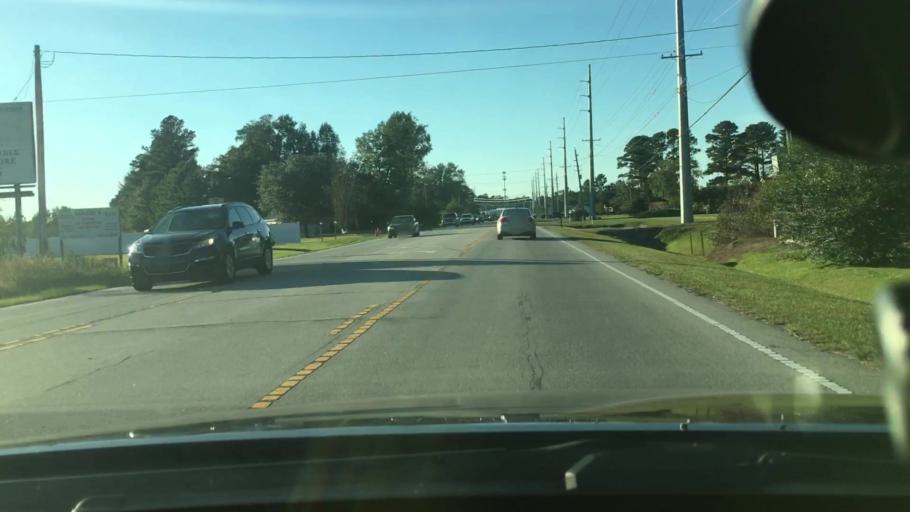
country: US
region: North Carolina
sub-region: Pitt County
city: Windsor
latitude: 35.5604
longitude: -77.3410
